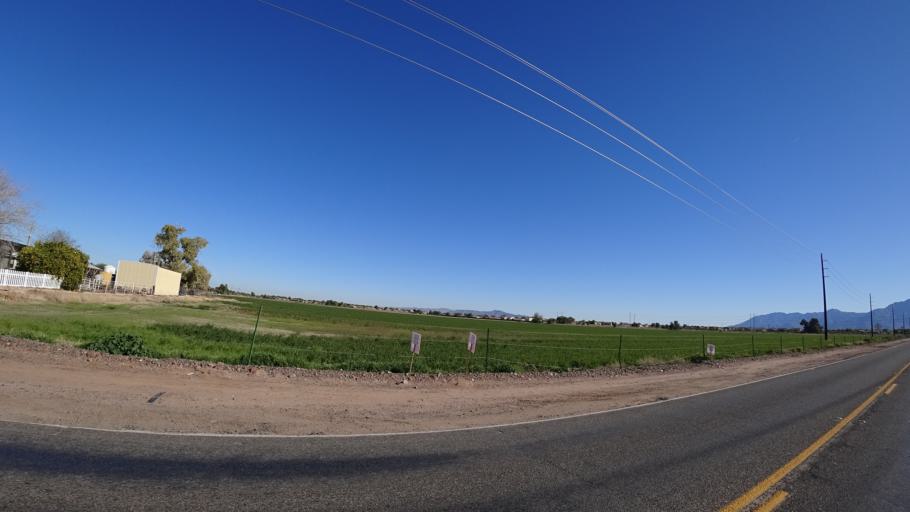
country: US
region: Arizona
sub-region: Maricopa County
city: Tolleson
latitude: 33.4205
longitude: -112.2897
